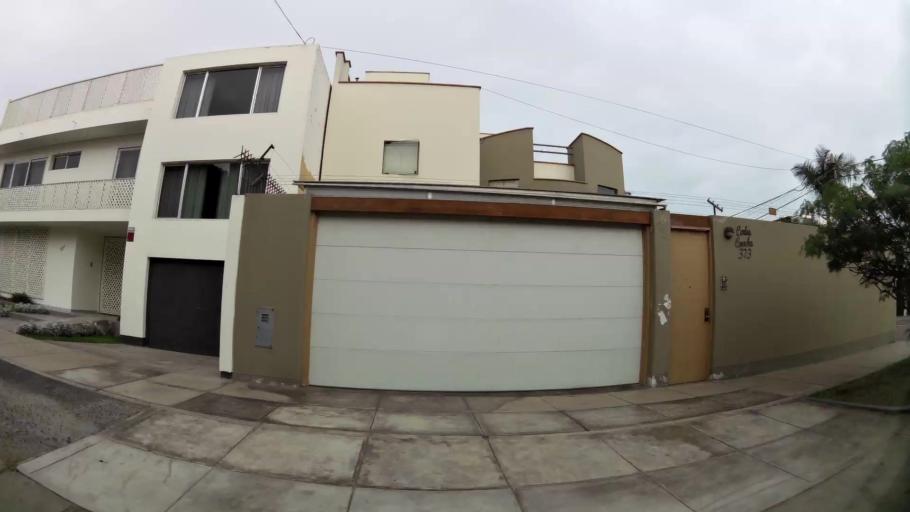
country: PE
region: Lima
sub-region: Lima
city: San Isidro
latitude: -12.1059
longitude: -77.0576
